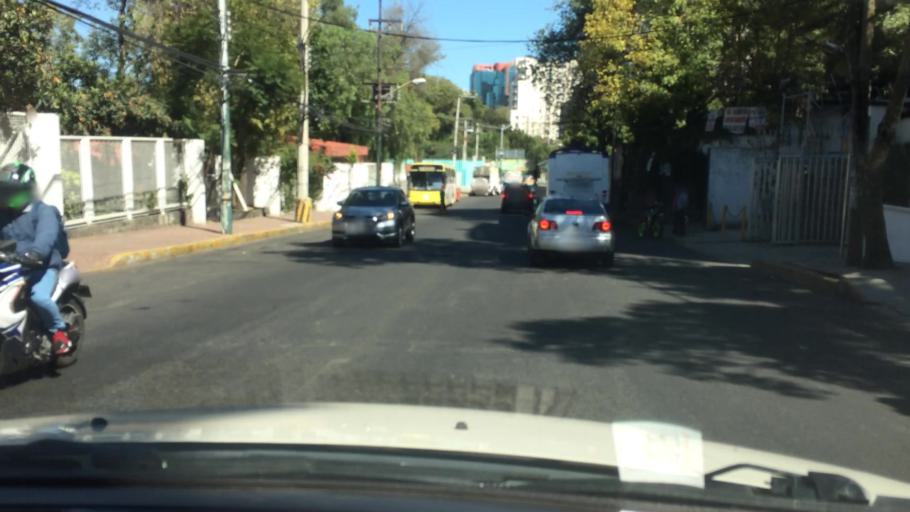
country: MX
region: Mexico City
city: Magdalena Contreras
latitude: 19.3223
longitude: -99.2212
